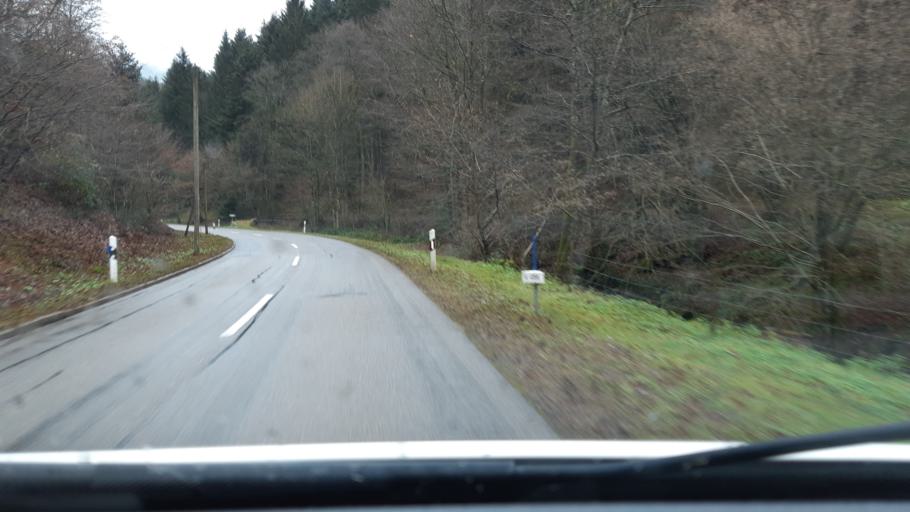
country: DE
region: Baden-Wuerttemberg
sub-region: Freiburg Region
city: Solden
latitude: 47.9076
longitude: 7.8257
